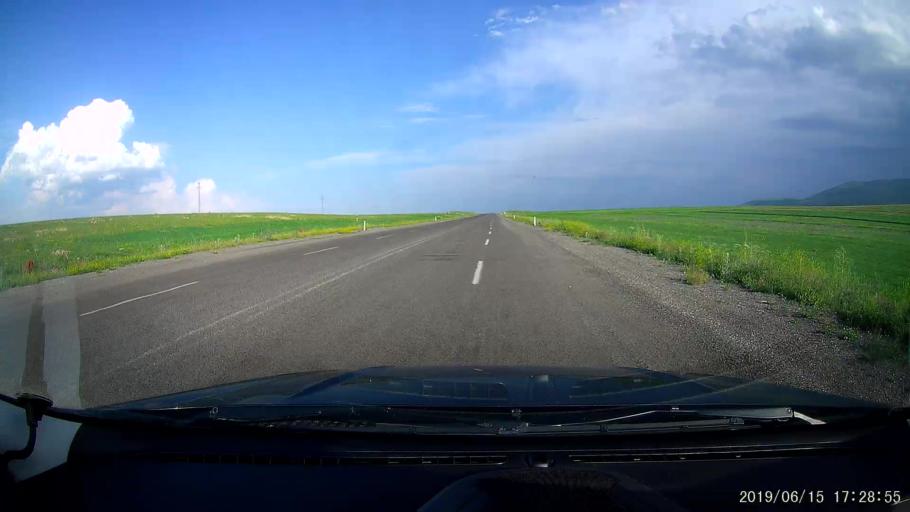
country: TR
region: Kars
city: Basgedikler
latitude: 40.5937
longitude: 43.4468
